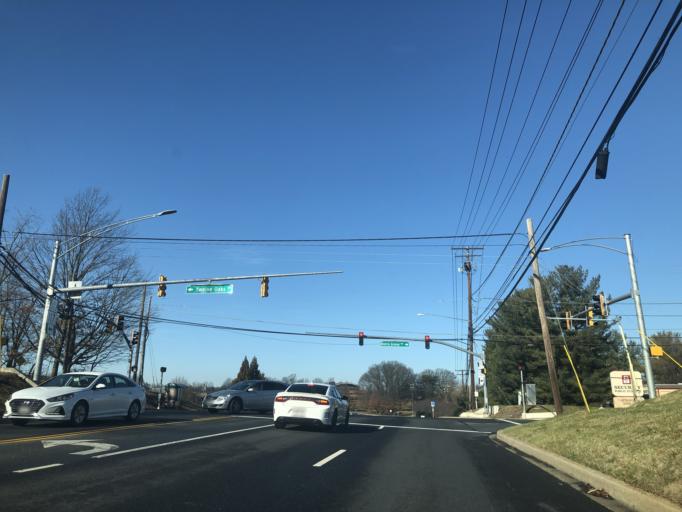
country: US
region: Maryland
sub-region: Montgomery County
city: Gaithersburg
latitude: 39.1458
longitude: -77.2278
